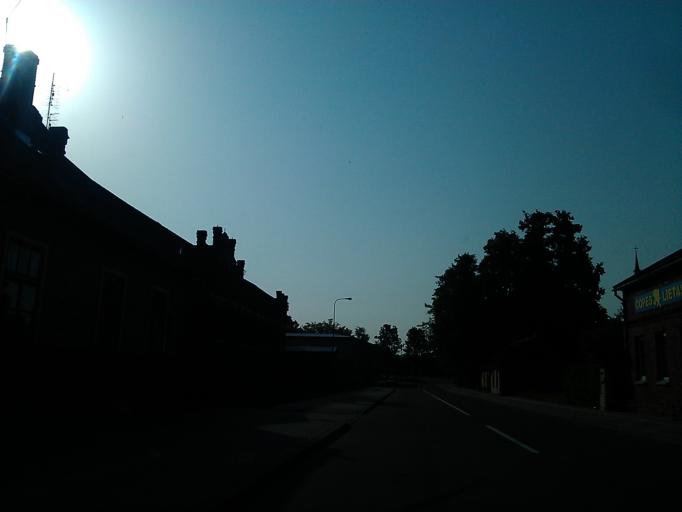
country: LV
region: Aizpute
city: Aizpute
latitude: 56.7166
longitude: 21.6126
